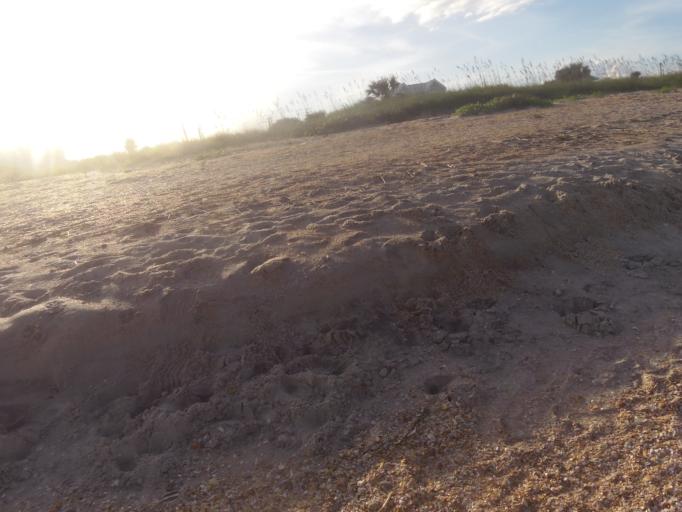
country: US
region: Florida
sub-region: Saint Johns County
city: Villano Beach
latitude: 29.9226
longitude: -81.2927
